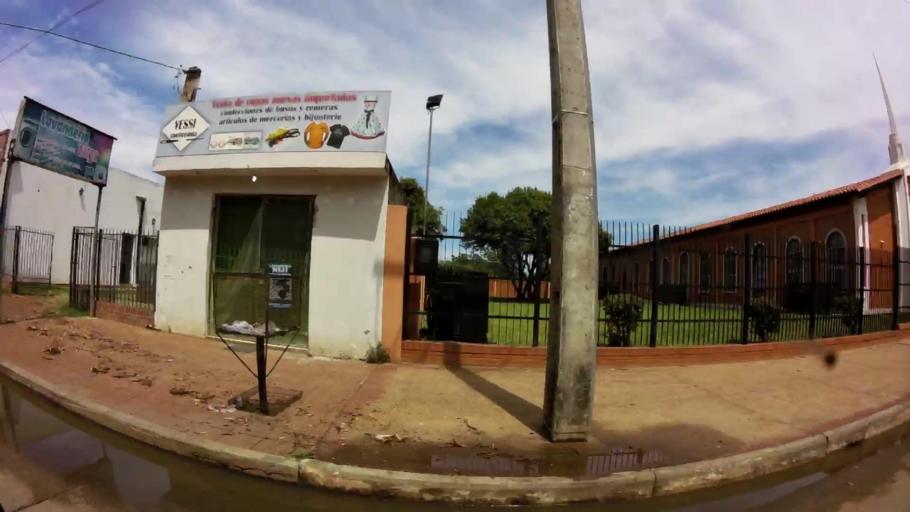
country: PY
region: Central
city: Limpio
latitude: -25.1685
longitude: -57.4764
